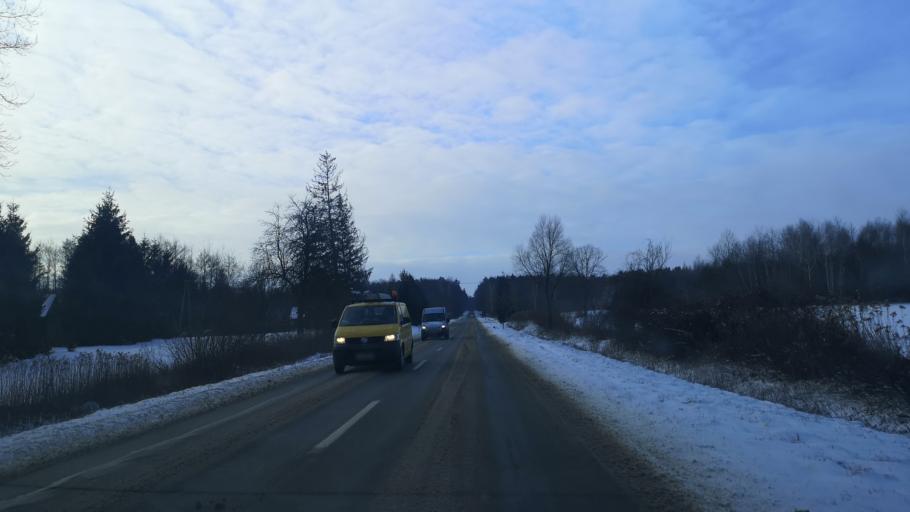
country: PL
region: Subcarpathian Voivodeship
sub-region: Powiat przeworski
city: Sieniawa
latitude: 50.2209
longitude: 22.6502
